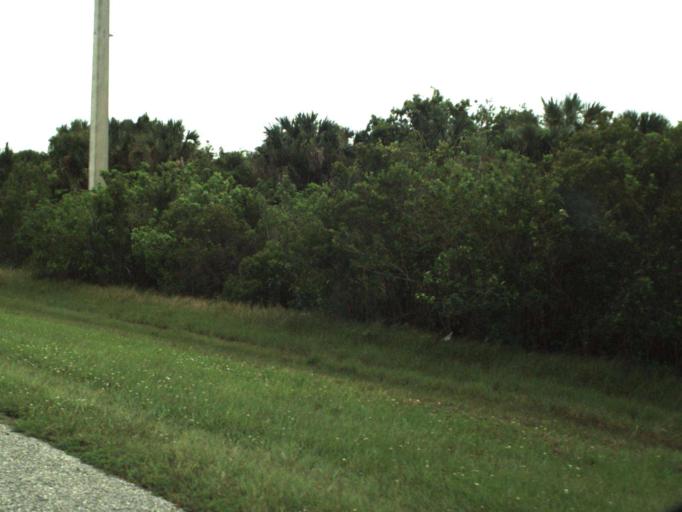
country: US
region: Florida
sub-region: Brevard County
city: Titusville
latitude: 28.5507
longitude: -80.8807
